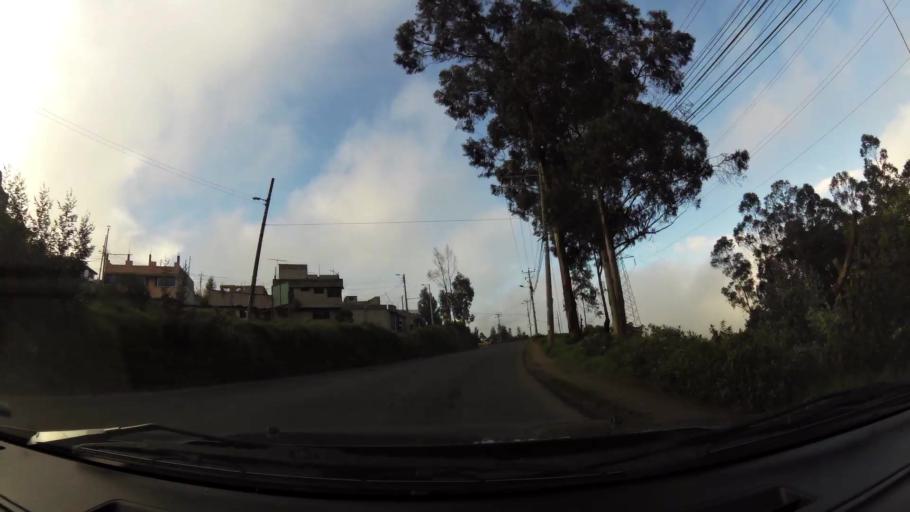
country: EC
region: Pichincha
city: Quito
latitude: -0.2591
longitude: -78.4949
